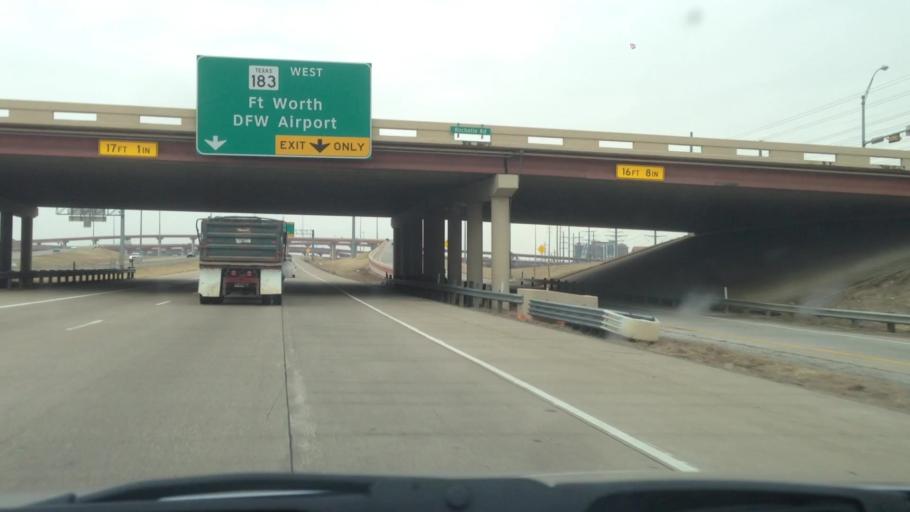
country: US
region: Texas
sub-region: Tarrant County
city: Euless
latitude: 32.8458
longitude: -97.0171
